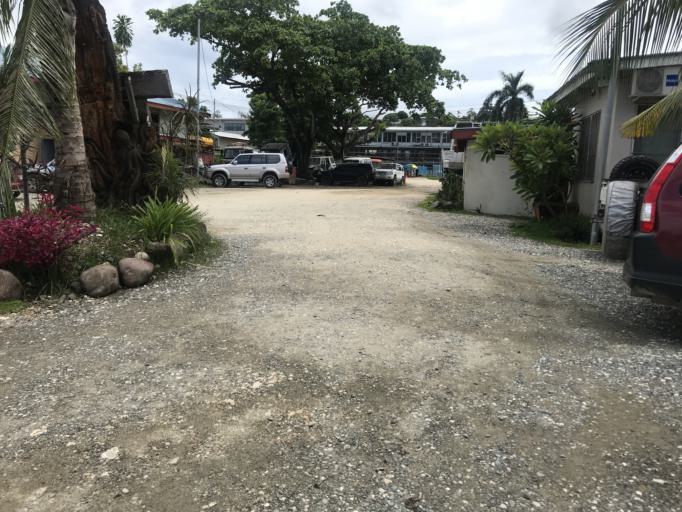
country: SB
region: Guadalcanal
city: Honiara
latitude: -9.4290
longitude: 159.9516
